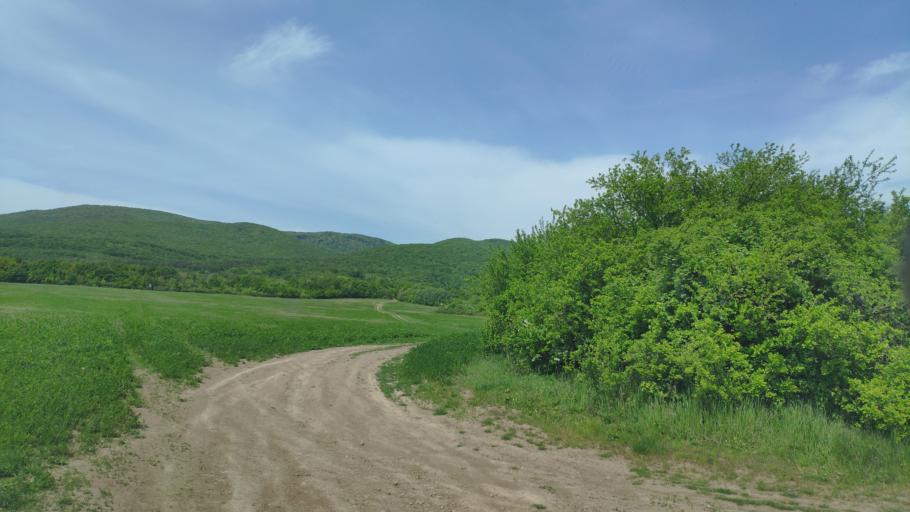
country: SK
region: Kosicky
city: Secovce
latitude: 48.6919
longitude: 21.5989
